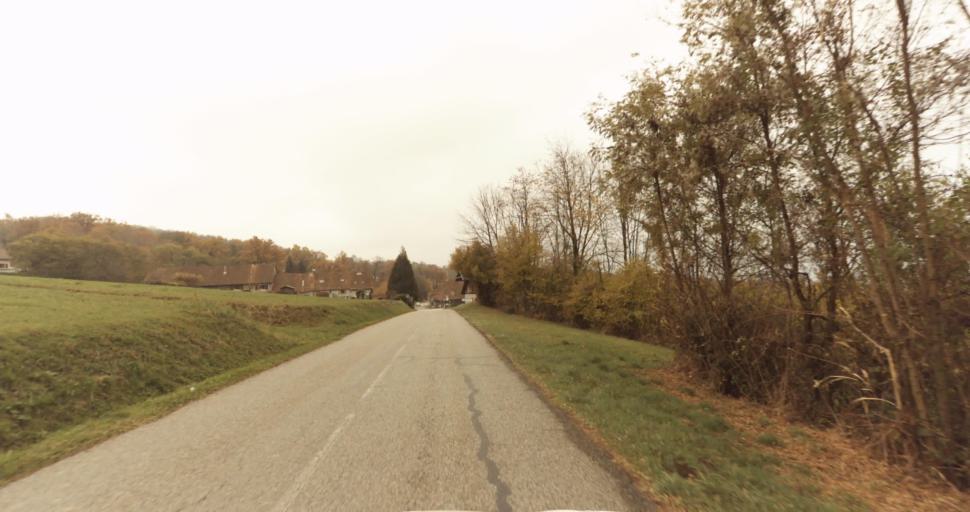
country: FR
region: Rhone-Alpes
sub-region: Departement de la Haute-Savoie
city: Saint-Felix
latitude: 45.7965
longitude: 5.9939
